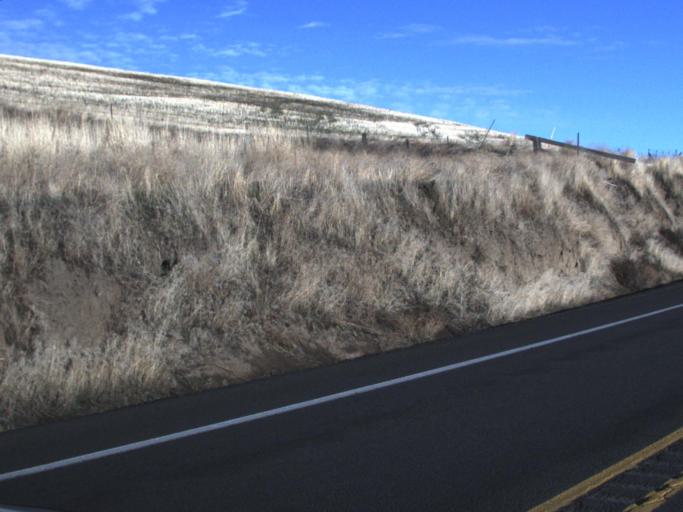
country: US
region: Washington
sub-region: Garfield County
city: Pomeroy
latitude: 46.7071
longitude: -117.7847
